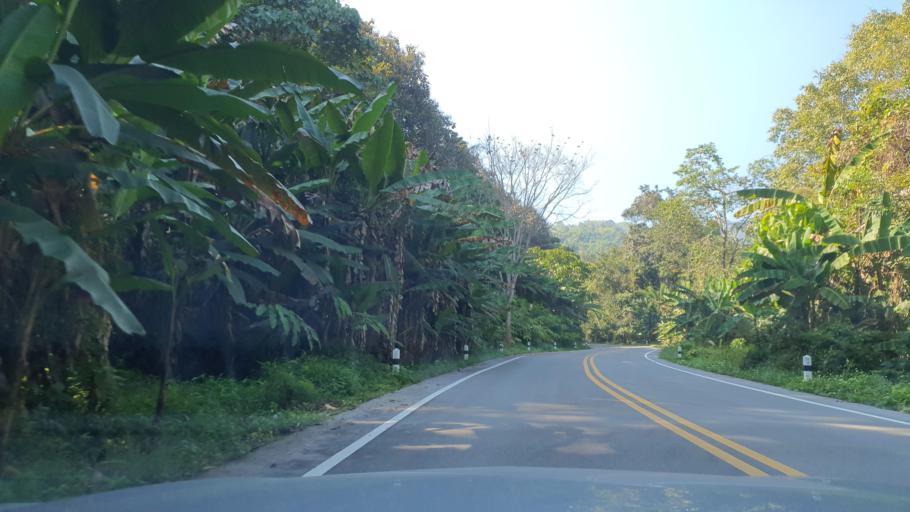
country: TH
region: Chiang Rai
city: Mae Lao
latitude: 19.8685
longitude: 99.6450
